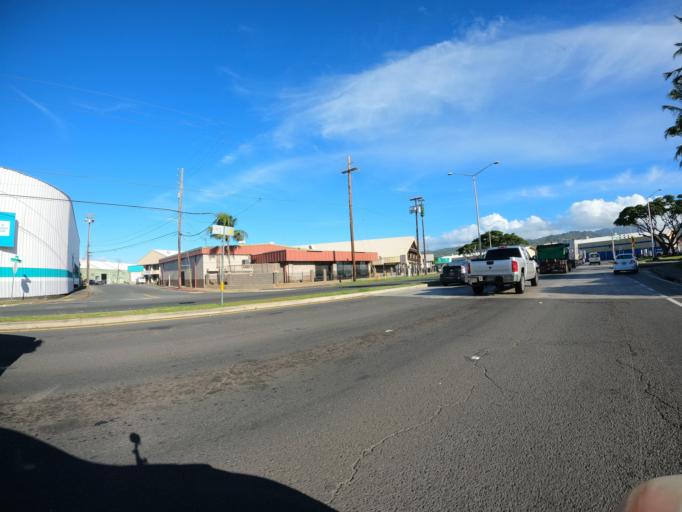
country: US
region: Hawaii
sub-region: Honolulu County
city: Honolulu
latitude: 21.3278
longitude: -157.8874
